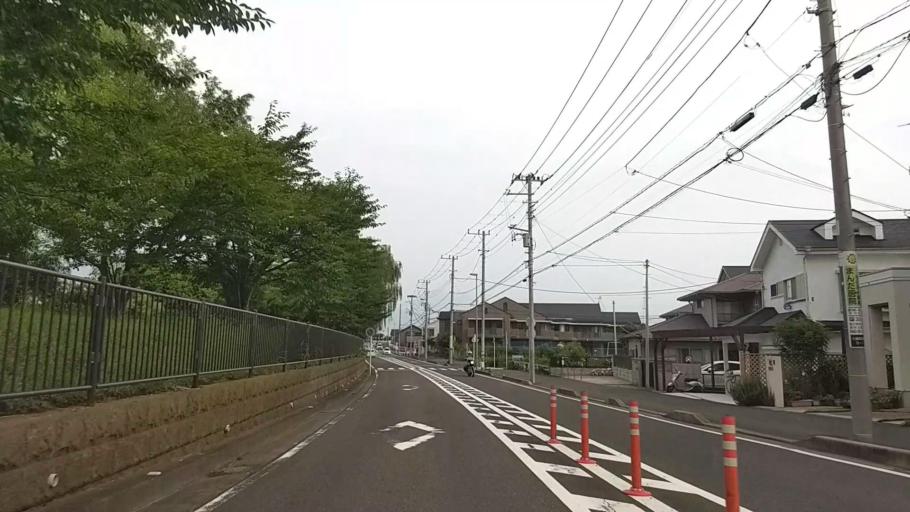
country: JP
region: Kanagawa
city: Hiratsuka
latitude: 35.3246
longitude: 139.3289
